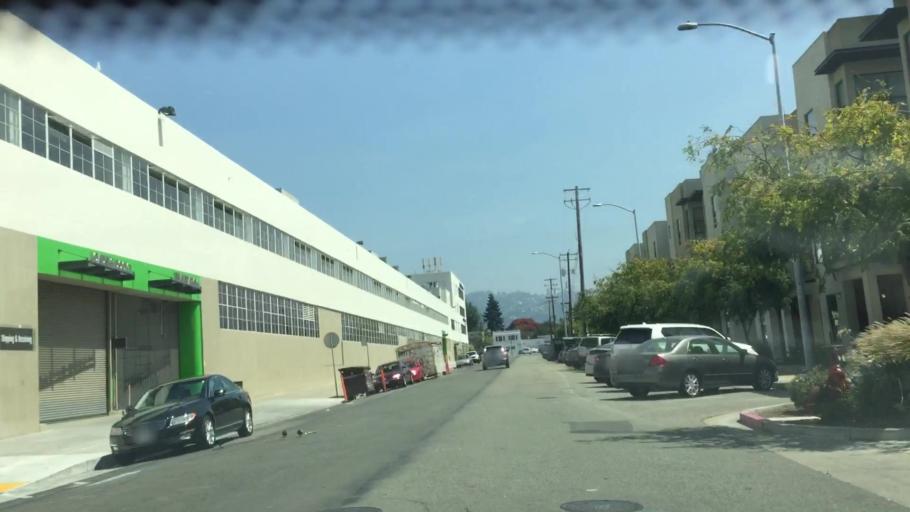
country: US
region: California
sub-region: Alameda County
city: Emeryville
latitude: 37.8495
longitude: -122.2887
